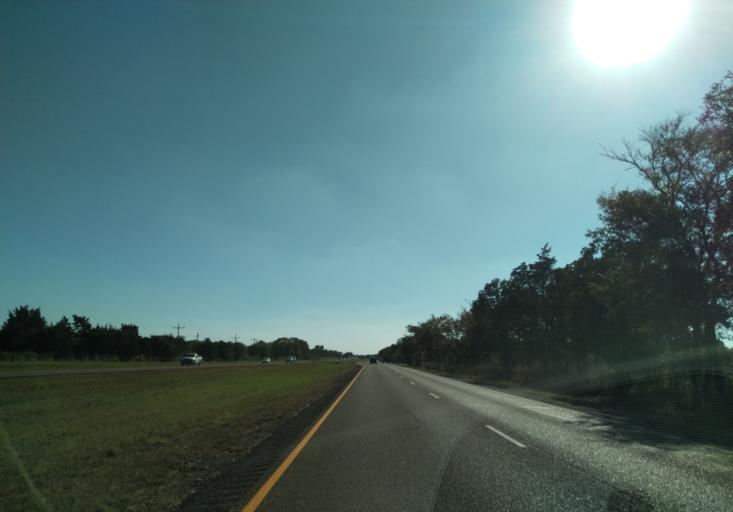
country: US
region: Texas
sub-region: Waller County
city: Hempstead
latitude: 30.2429
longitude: -96.0492
